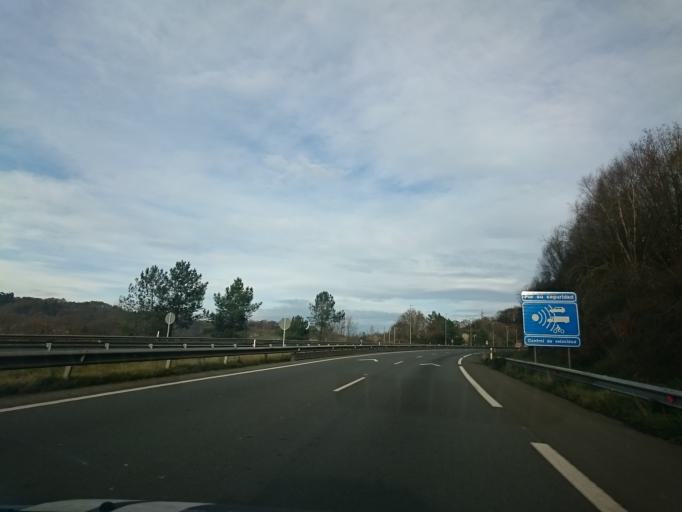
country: ES
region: Asturias
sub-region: Province of Asturias
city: Castandiello
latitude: 43.3199
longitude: -5.8699
